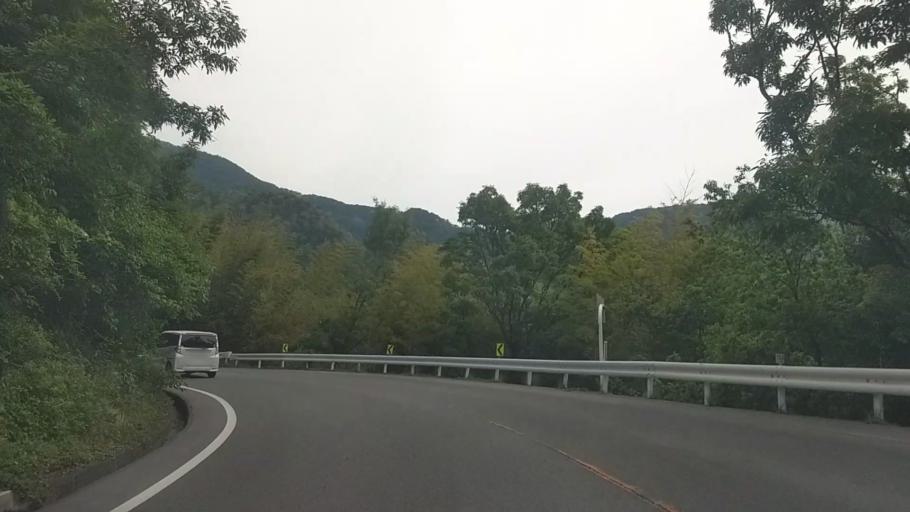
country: JP
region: Yamanashi
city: Isawa
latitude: 35.5668
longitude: 138.5926
